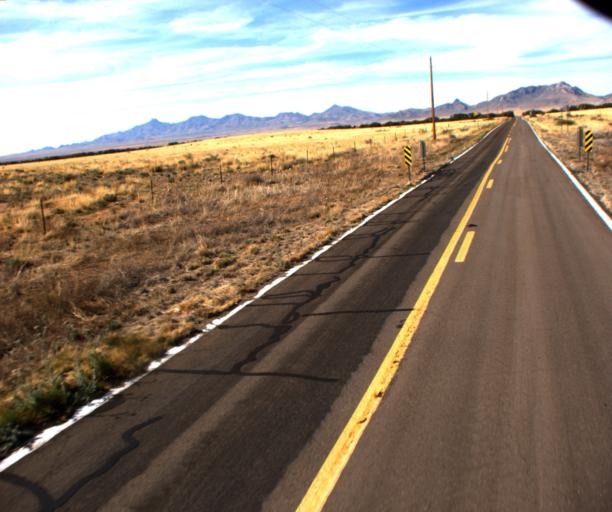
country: US
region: Arizona
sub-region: Cochise County
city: Willcox
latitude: 31.9958
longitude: -109.4400
